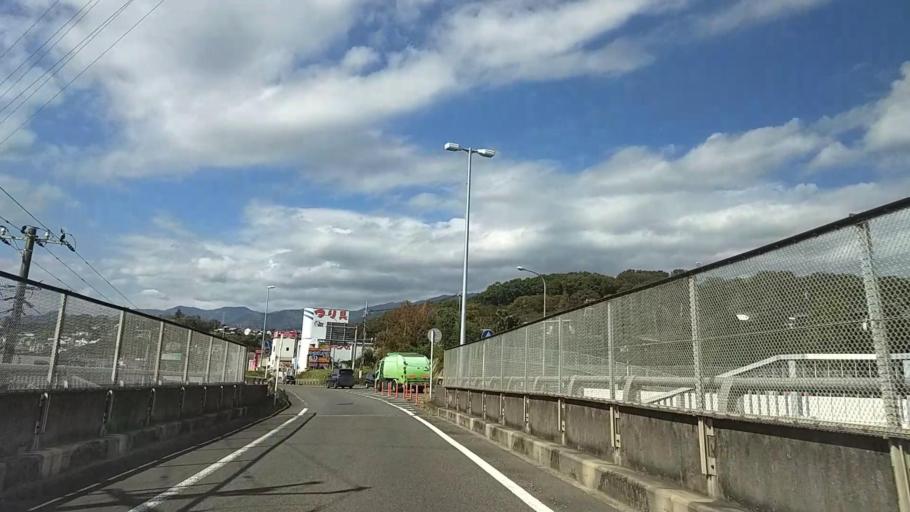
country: JP
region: Kanagawa
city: Hadano
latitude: 35.3801
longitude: 139.2325
